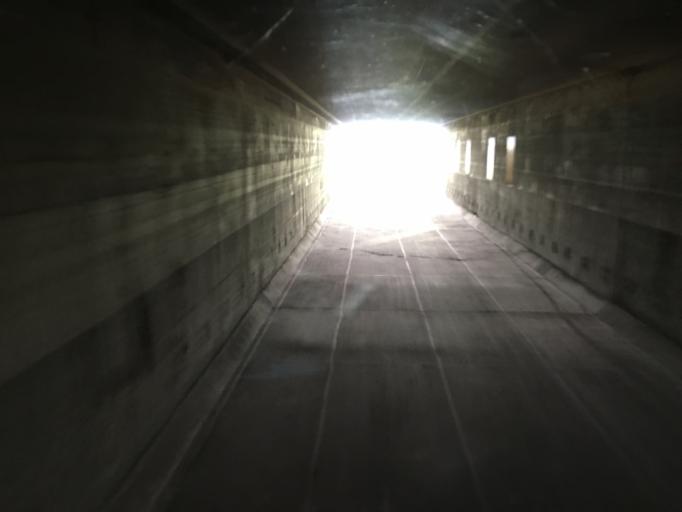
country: IT
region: Piedmont
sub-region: Provincia di Cuneo
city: Sambuco
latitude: 44.2027
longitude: 7.0938
